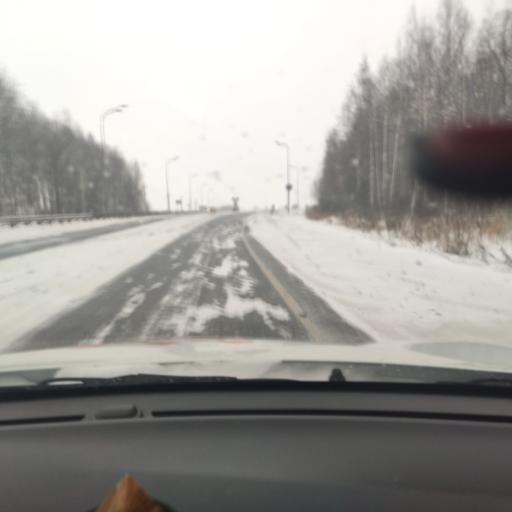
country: RU
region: Tatarstan
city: Verkhniy Uslon
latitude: 55.7110
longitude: 48.8865
